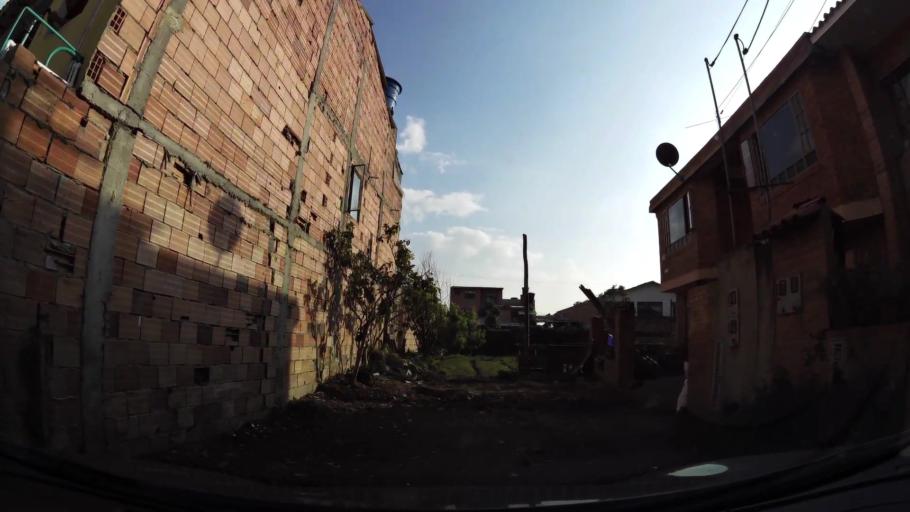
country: CO
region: Cundinamarca
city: Cota
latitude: 4.8131
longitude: -74.1007
